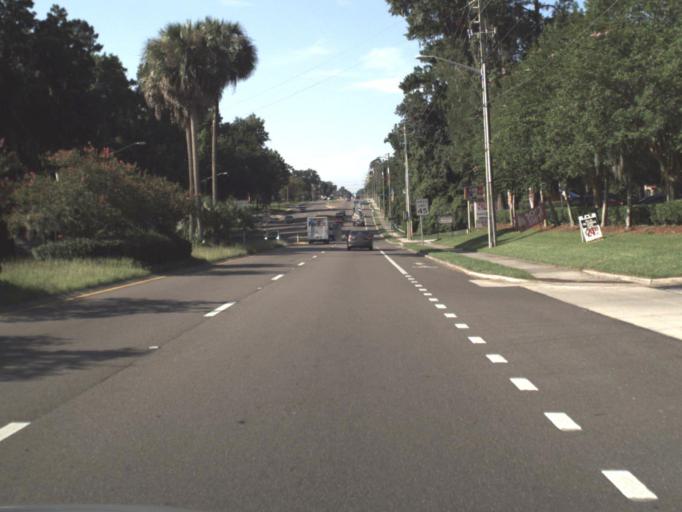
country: US
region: Florida
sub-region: Alachua County
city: Gainesville
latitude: 29.6870
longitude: -82.3391
